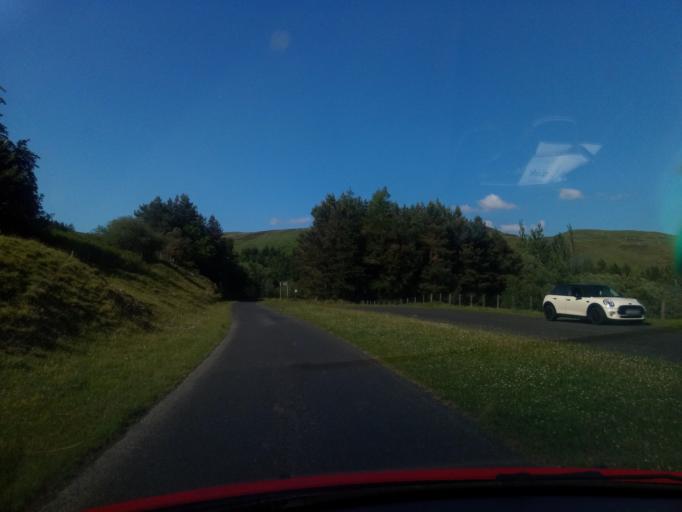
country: GB
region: Scotland
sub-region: The Scottish Borders
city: Peebles
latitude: 55.4964
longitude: -3.2592
